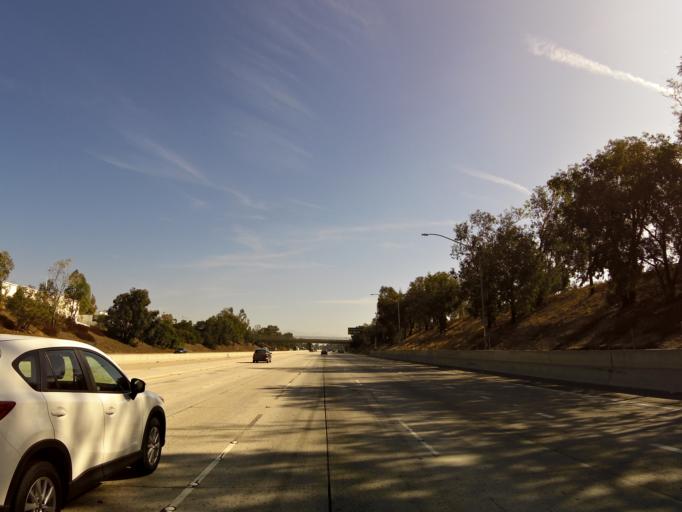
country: US
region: California
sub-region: Los Angeles County
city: Chatsworth
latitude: 34.2733
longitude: -118.5658
